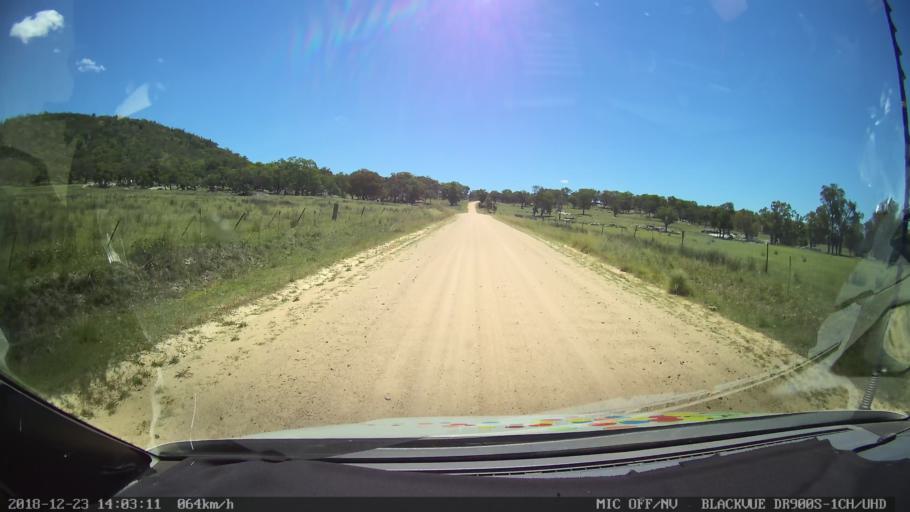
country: AU
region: New South Wales
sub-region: Tamworth Municipality
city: Manilla
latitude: -30.6242
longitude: 151.1032
